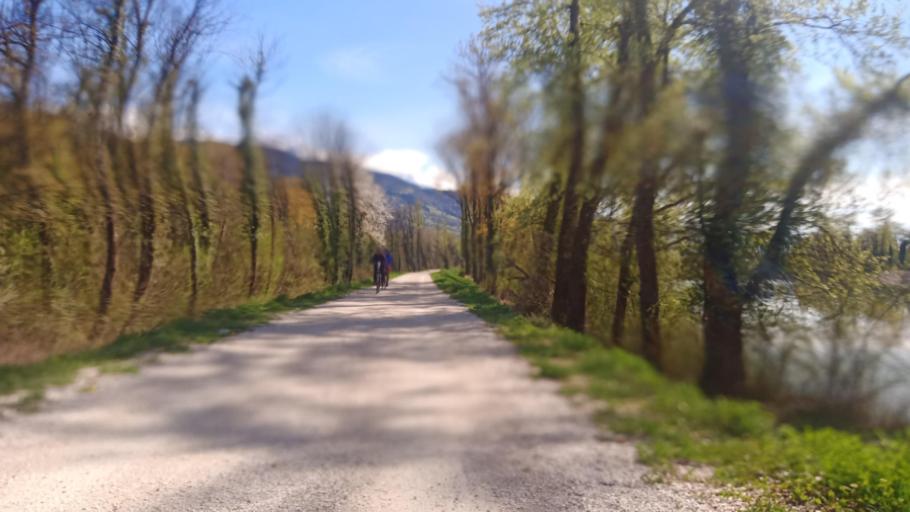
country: FR
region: Rhone-Alpes
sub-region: Departement de l'Isere
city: Le Champ-pres-Froges
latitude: 45.2982
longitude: 5.9330
